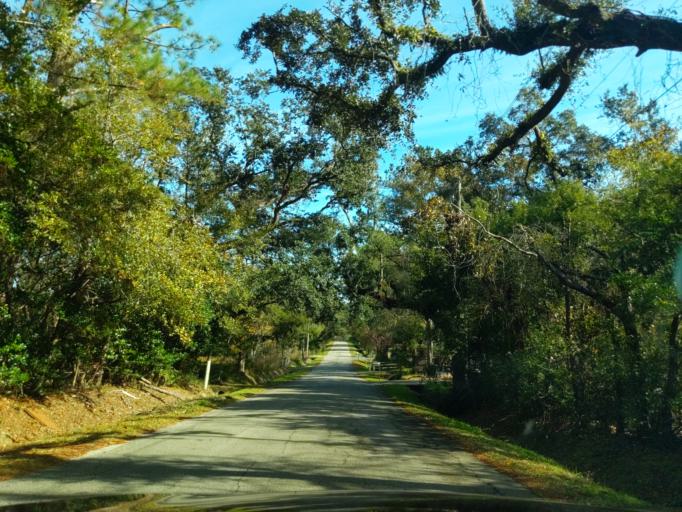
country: US
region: Florida
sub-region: Leon County
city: Tallahassee
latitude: 30.4695
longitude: -84.3391
